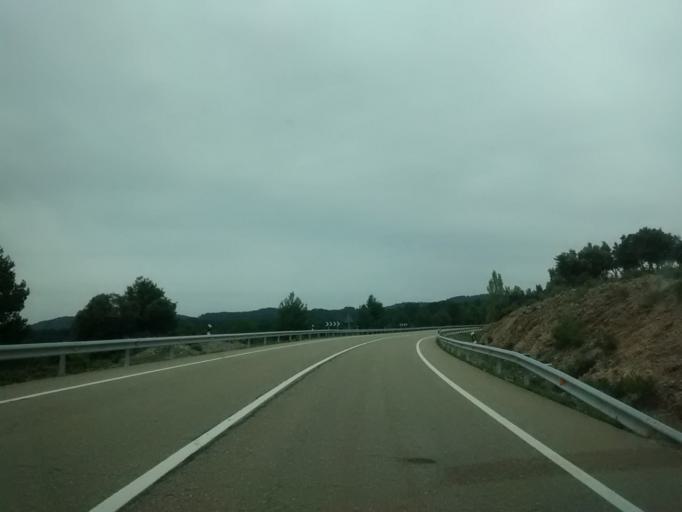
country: ES
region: Aragon
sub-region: Provincia de Teruel
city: Fornoles
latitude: 40.8742
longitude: -0.0266
